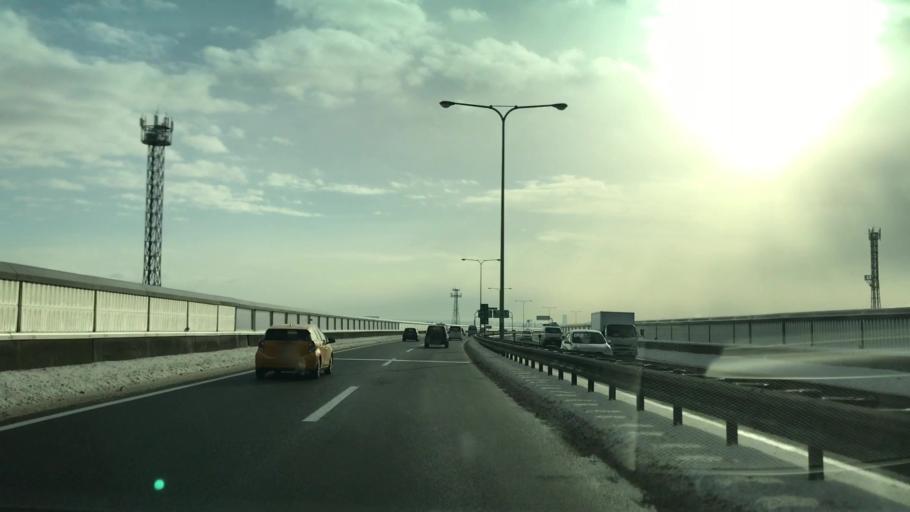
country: JP
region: Hokkaido
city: Sapporo
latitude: 43.0893
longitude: 141.4130
